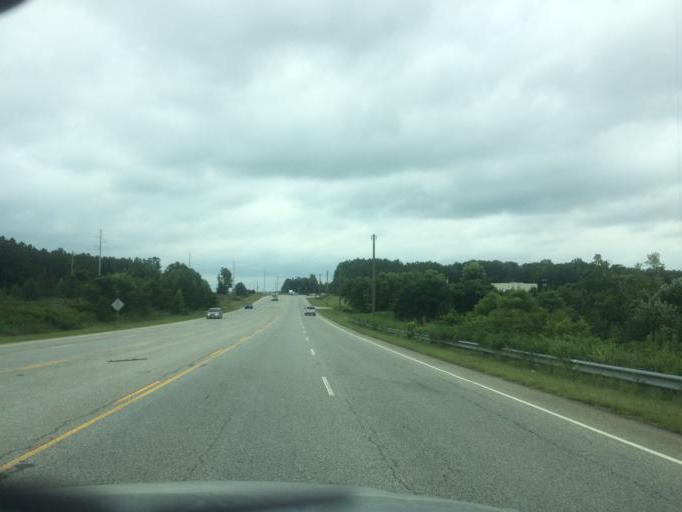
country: US
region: South Carolina
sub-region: Greenville County
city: Greer
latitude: 34.9029
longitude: -82.1925
